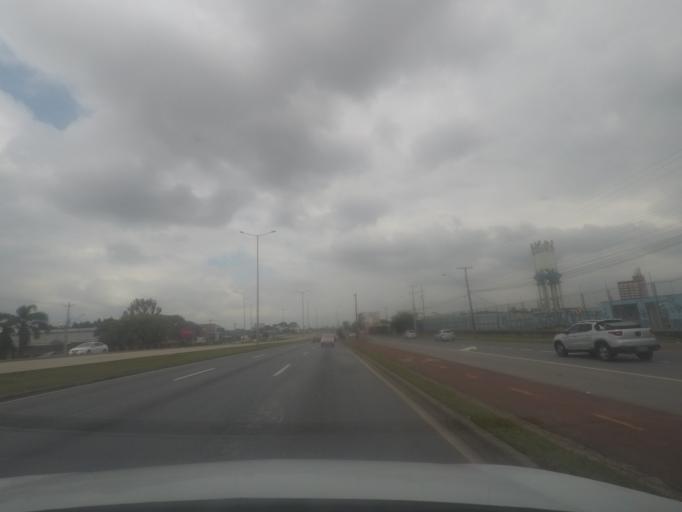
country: BR
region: Parana
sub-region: Sao Jose Dos Pinhais
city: Sao Jose dos Pinhais
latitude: -25.5159
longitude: -49.2913
